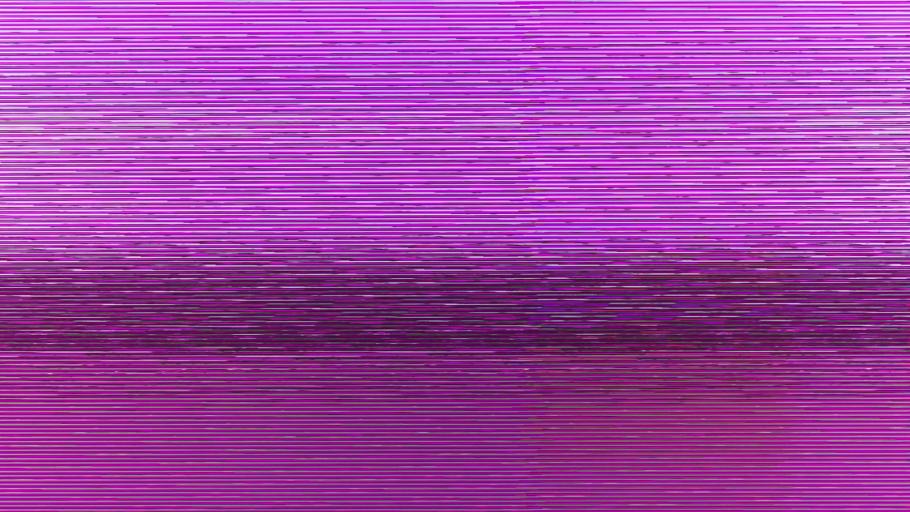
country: US
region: Michigan
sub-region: Genesee County
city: Grand Blanc
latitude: 42.9450
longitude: -83.6321
